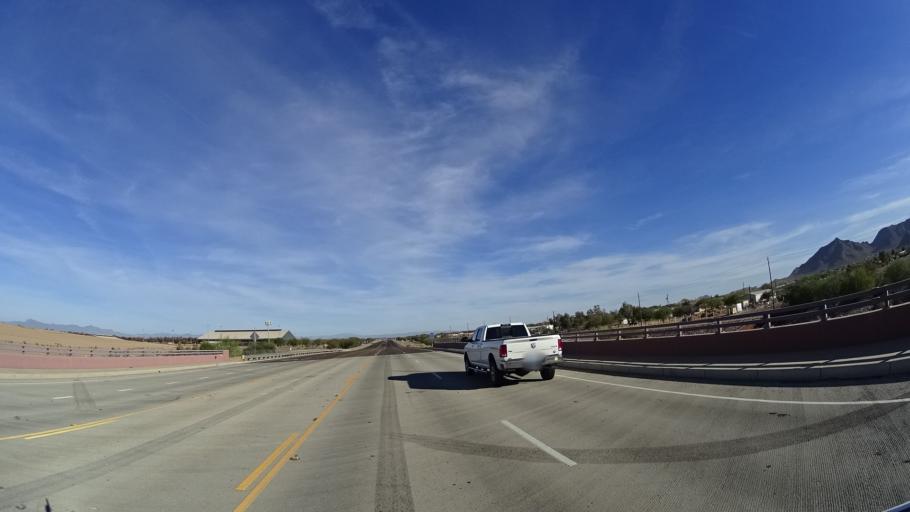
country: US
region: Arizona
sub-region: Maricopa County
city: Queen Creek
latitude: 33.2195
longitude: -111.6483
